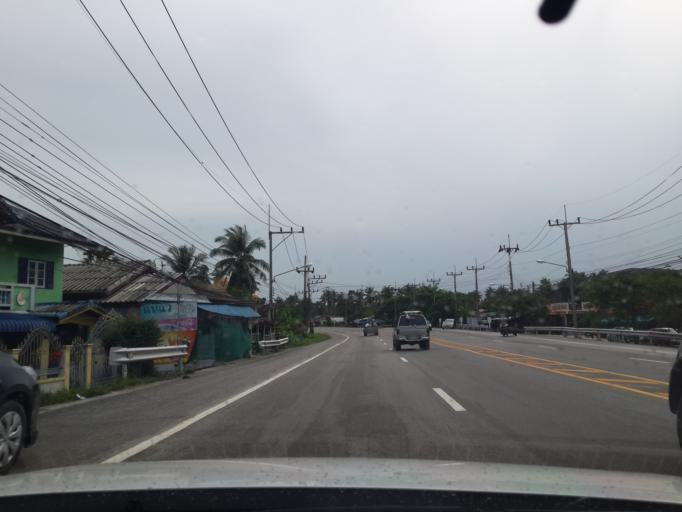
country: TH
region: Pattani
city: Nong Chik
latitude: 6.8479
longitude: 101.1869
